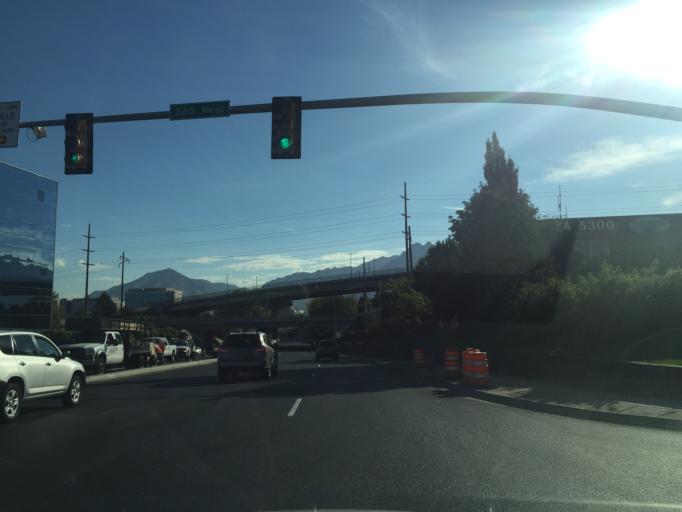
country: US
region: Utah
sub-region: Salt Lake County
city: Murray
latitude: 40.6548
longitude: -111.9000
